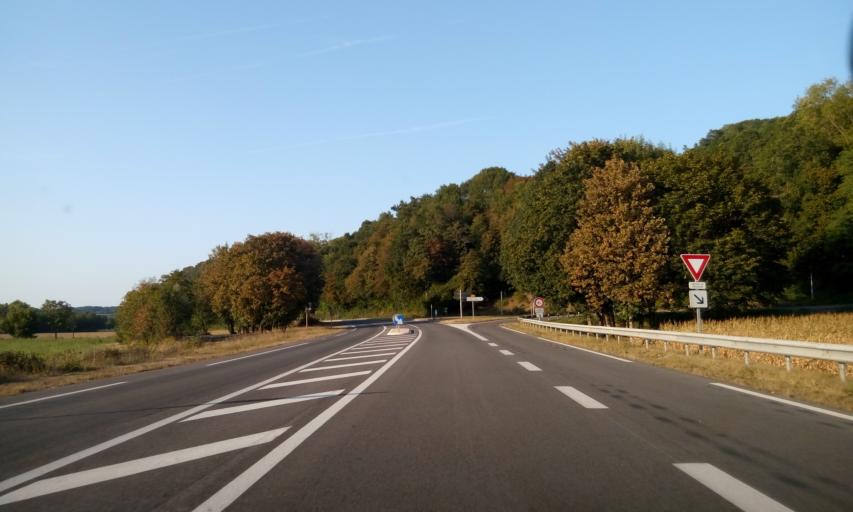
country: FR
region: Rhone-Alpes
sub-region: Departement de l'Ain
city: Neuville-sur-Ain
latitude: 46.0571
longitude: 5.3858
